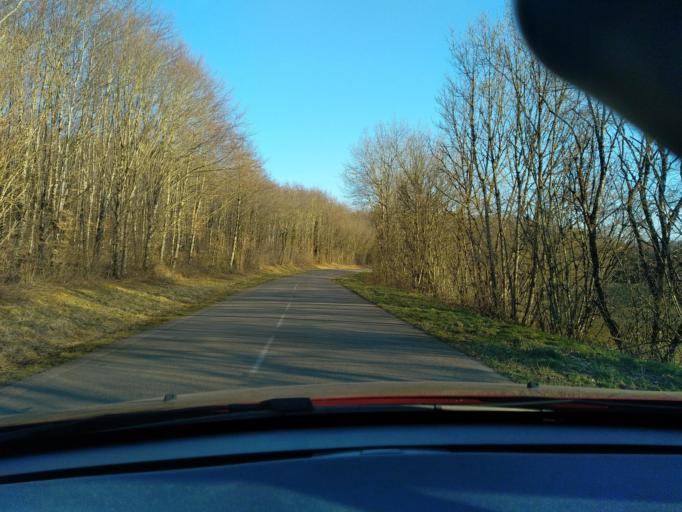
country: FR
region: Franche-Comte
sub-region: Departement du Jura
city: Perrigny
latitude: 46.6170
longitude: 5.6419
